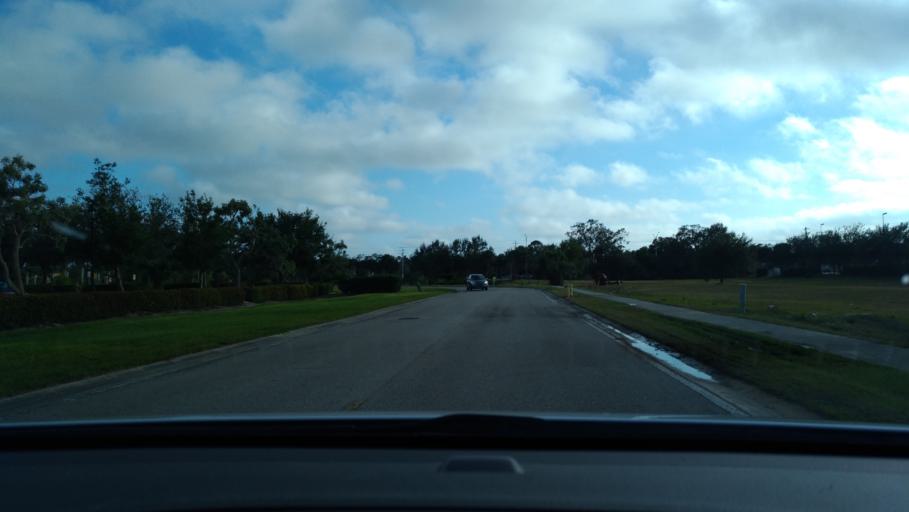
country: US
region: Florida
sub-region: Lee County
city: Estero
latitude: 26.4335
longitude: -81.7875
